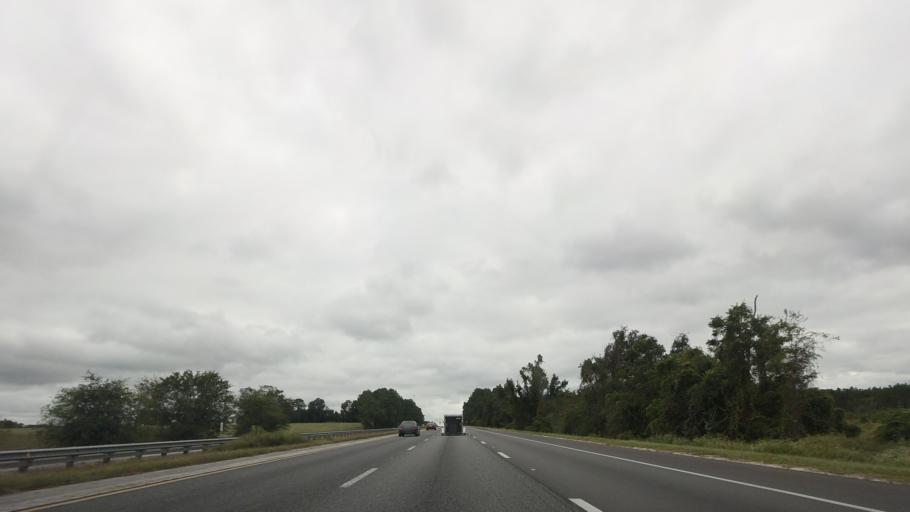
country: US
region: Florida
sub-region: Alachua County
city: High Springs
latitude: 29.8844
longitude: -82.5444
